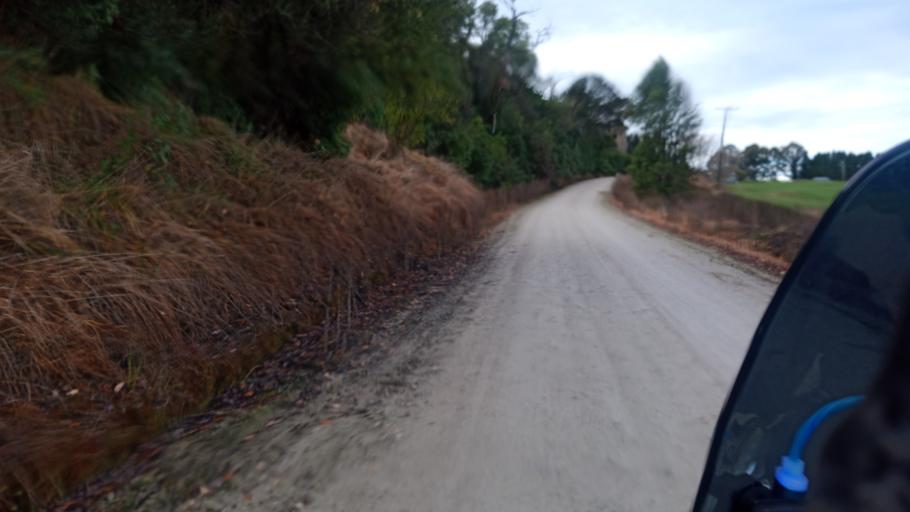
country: NZ
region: Gisborne
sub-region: Gisborne District
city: Gisborne
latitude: -38.3817
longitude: 177.9608
